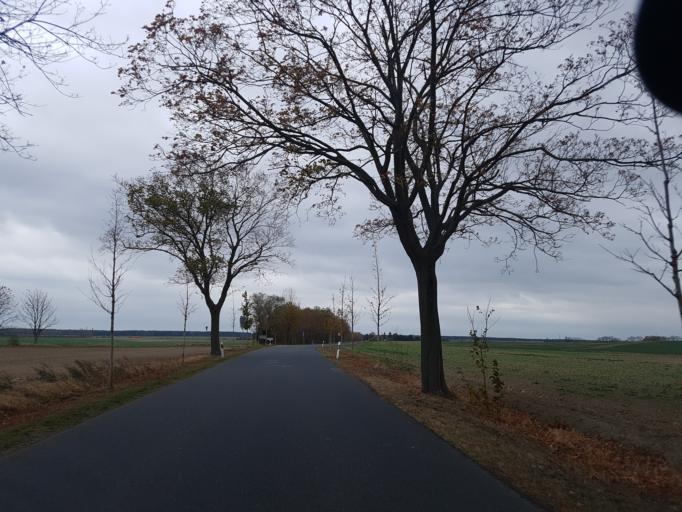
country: DE
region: Brandenburg
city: Juterbog
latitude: 51.9371
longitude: 13.0575
